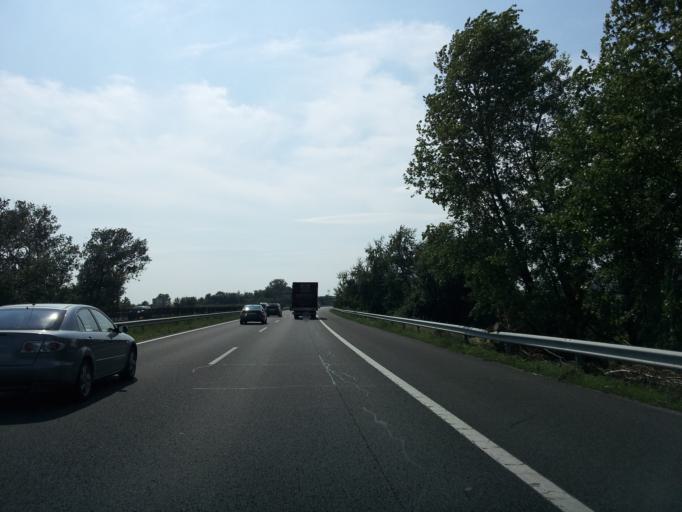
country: HU
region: Fejer
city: Velence
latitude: 47.2508
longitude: 18.6630
